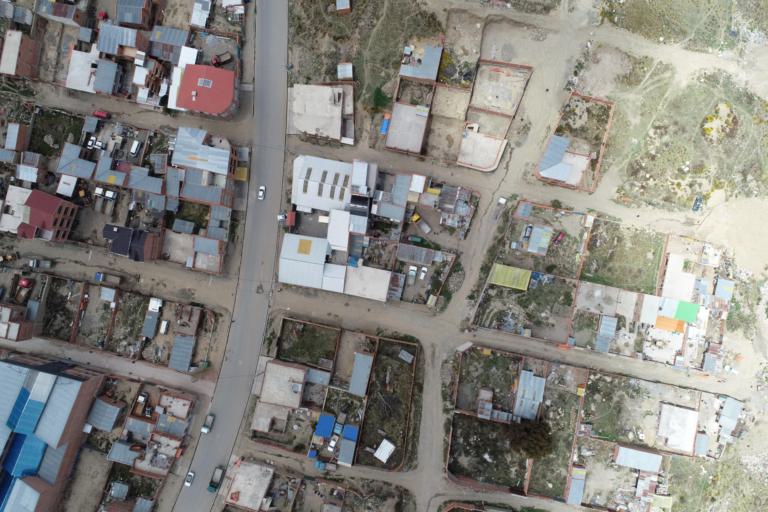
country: BO
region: La Paz
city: La Paz
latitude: -16.4422
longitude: -68.1452
